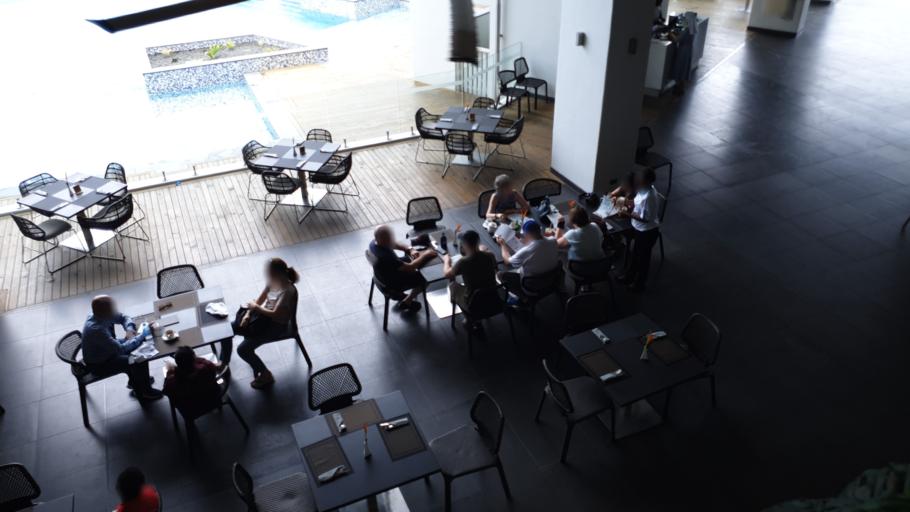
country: PG
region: National Capital
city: Port Moresby
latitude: -9.5345
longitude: 147.2901
